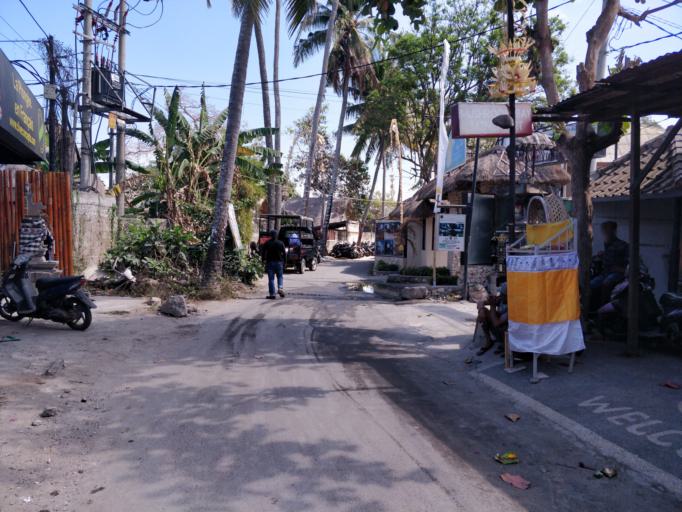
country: ID
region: Bali
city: Lembongan Kawan
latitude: -8.6836
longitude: 115.4338
